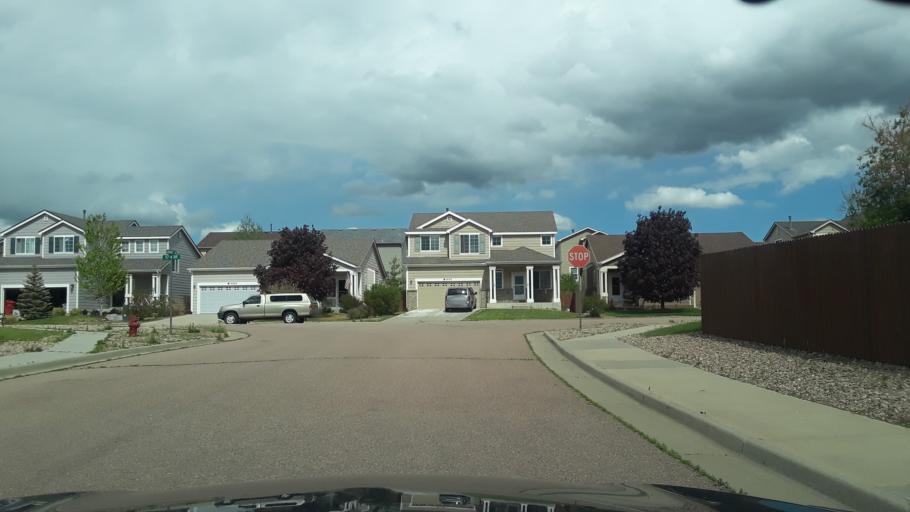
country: US
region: Colorado
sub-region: El Paso County
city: Gleneagle
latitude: 39.0369
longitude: -104.8346
